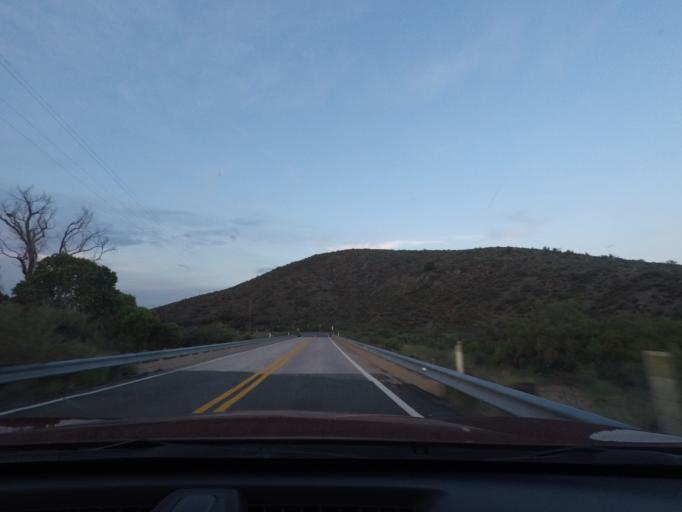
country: US
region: Arizona
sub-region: Yavapai County
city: Prescott
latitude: 34.4206
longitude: -112.7019
